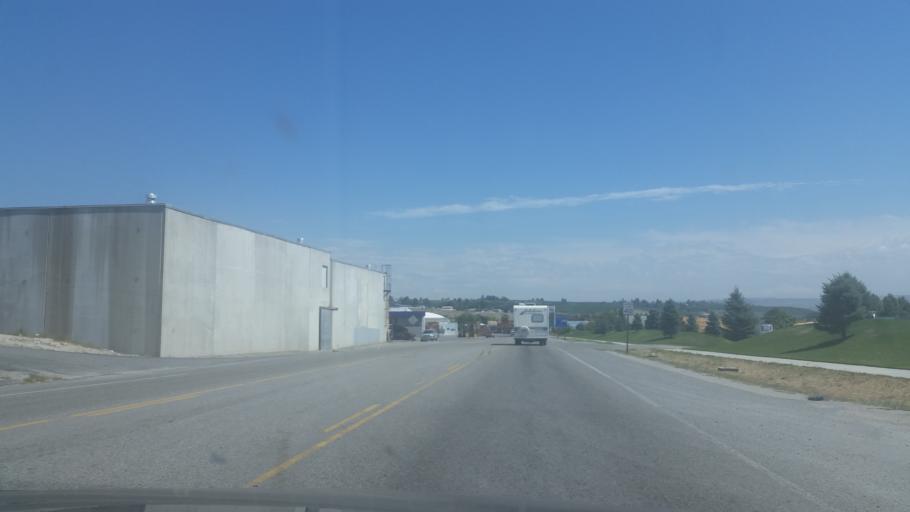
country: US
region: Washington
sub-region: Okanogan County
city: Brewster
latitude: 48.1021
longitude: -119.7856
